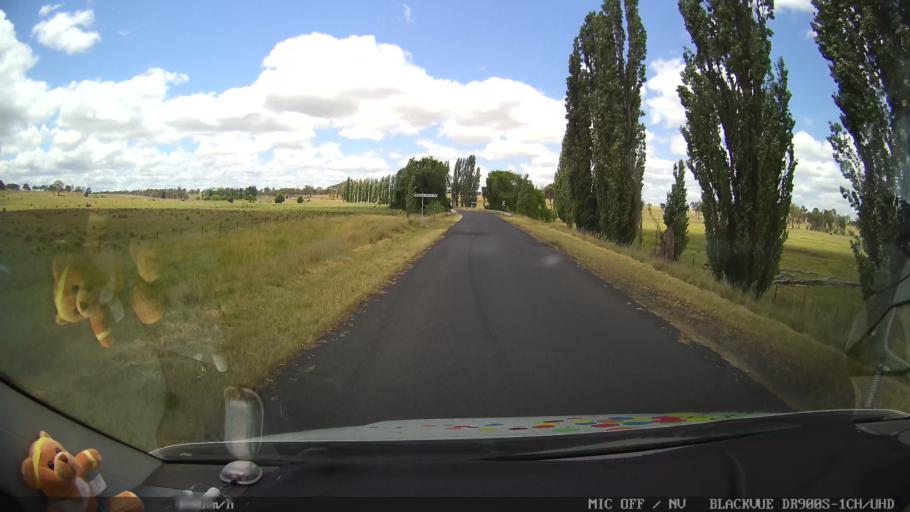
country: AU
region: New South Wales
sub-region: Glen Innes Severn
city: Glen Innes
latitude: -29.4345
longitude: 151.7554
